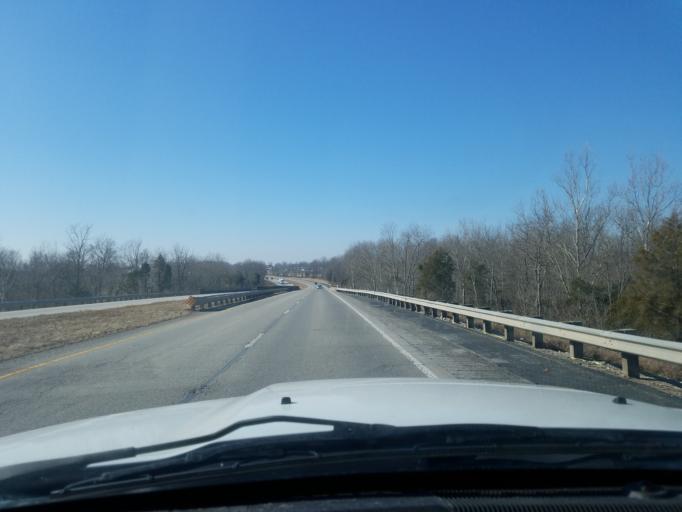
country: US
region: Kentucky
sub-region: Hardin County
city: Elizabethtown
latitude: 37.6493
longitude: -85.9046
